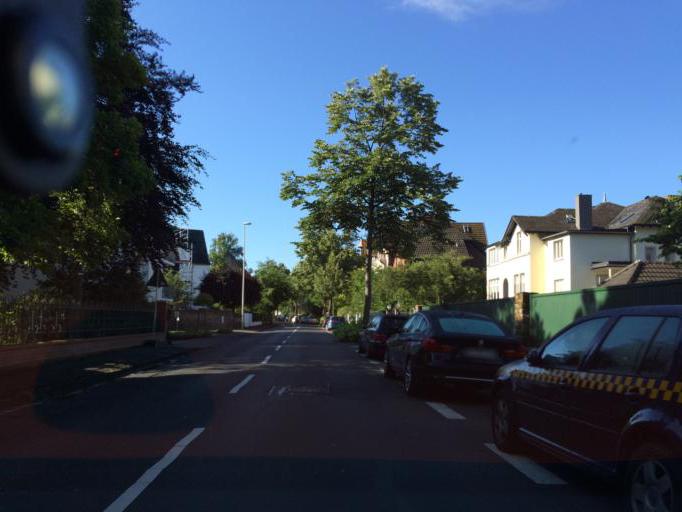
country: DE
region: North Rhine-Westphalia
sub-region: Regierungsbezirk Koln
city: Konigswinter
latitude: 50.6875
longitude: 7.1685
